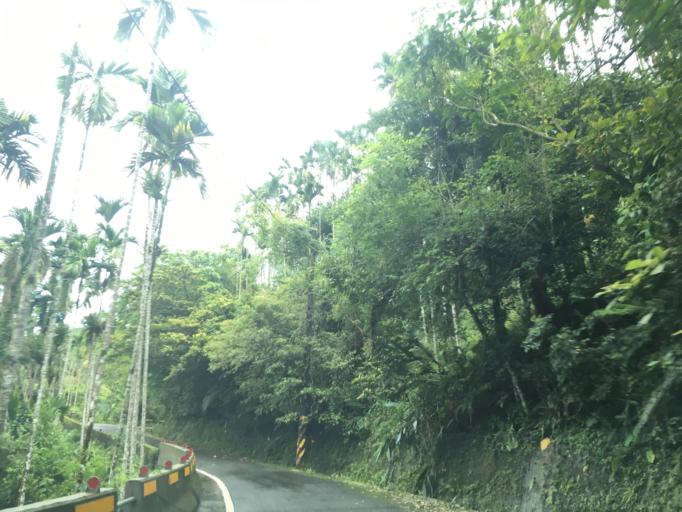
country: TW
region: Taiwan
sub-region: Yunlin
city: Douliu
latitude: 23.5664
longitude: 120.6449
